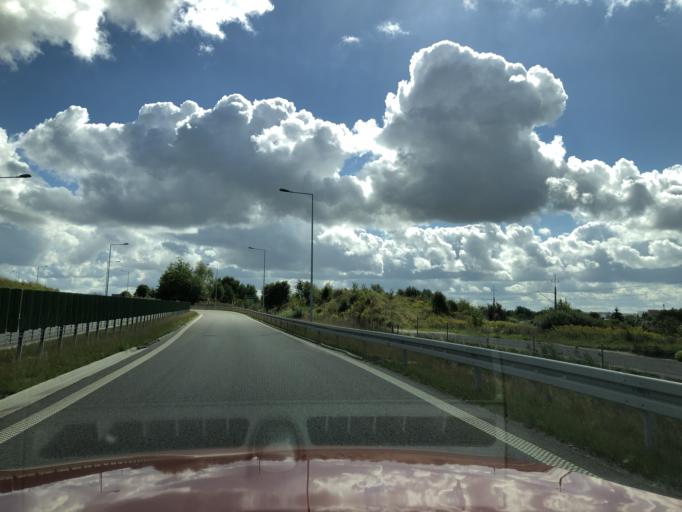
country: PL
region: West Pomeranian Voivodeship
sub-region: Powiat szczecinecki
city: Szczecinek
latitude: 53.7107
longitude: 16.7175
